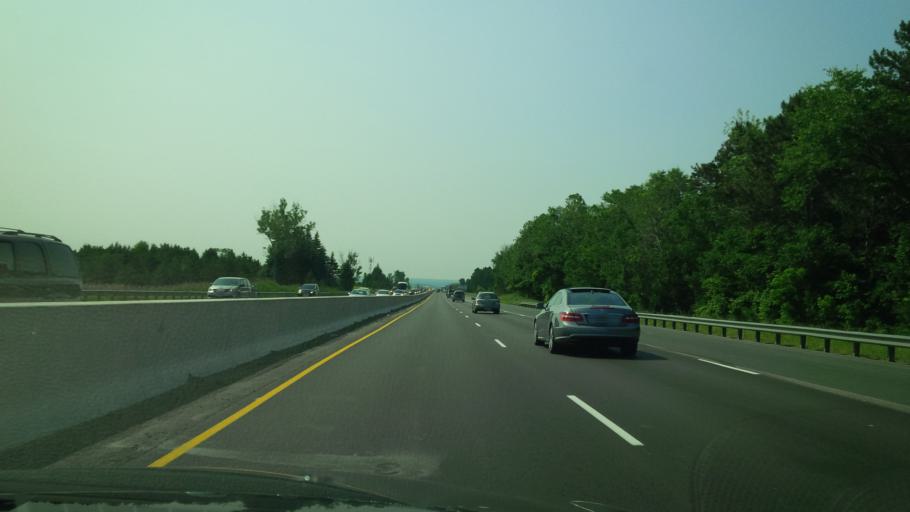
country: CA
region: Ontario
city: Bradford West Gwillimbury
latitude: 44.1349
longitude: -79.6396
